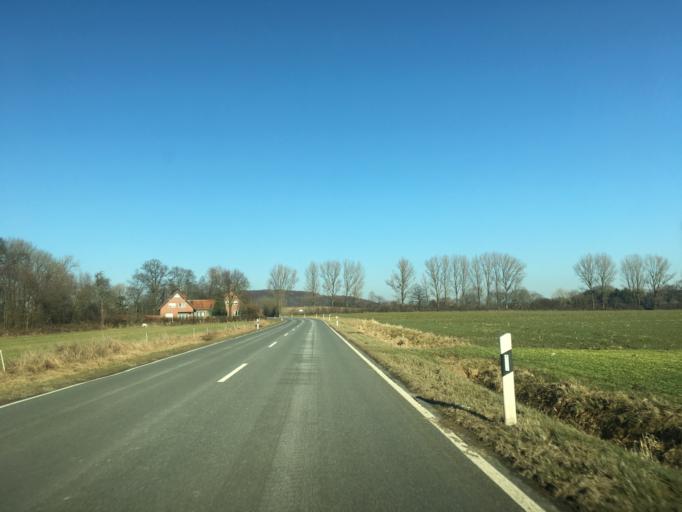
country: DE
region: North Rhine-Westphalia
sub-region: Regierungsbezirk Munster
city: Horstmar
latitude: 52.0642
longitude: 7.2851
